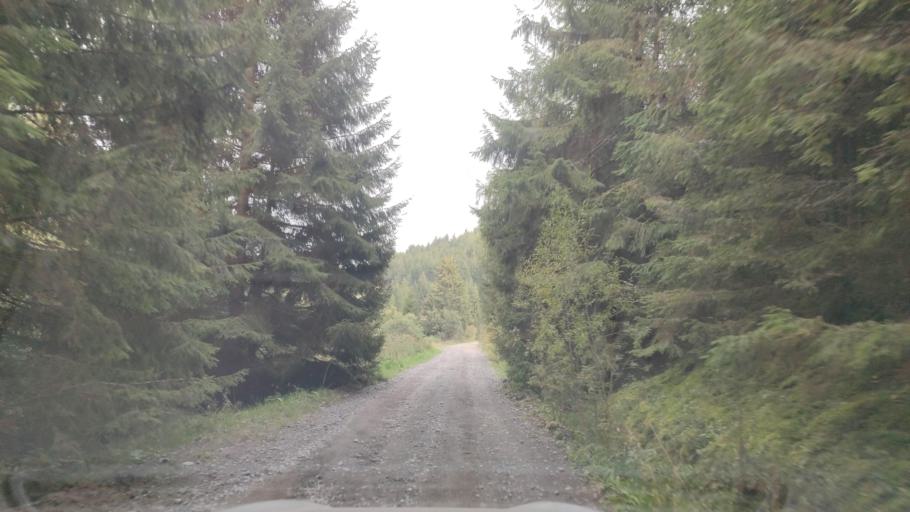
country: RO
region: Harghita
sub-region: Comuna Remetea
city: Remetea
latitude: 46.8123
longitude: 25.3603
